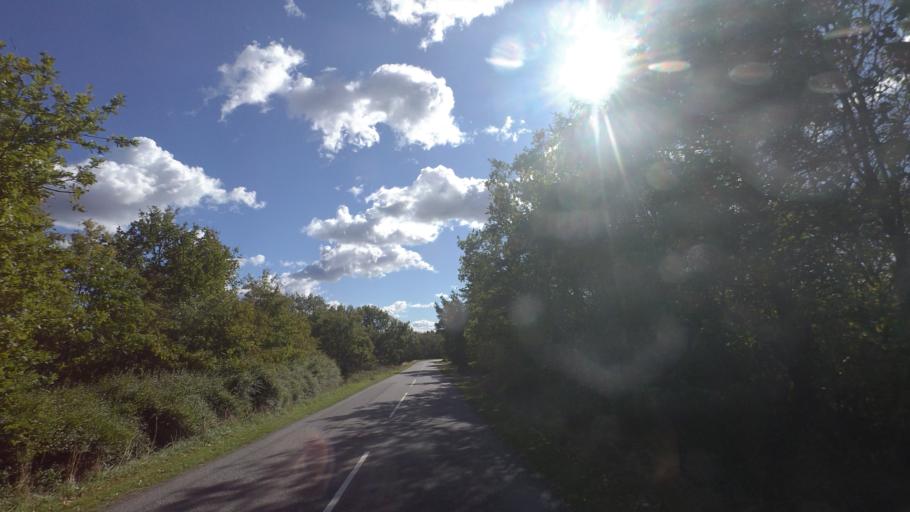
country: DK
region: Capital Region
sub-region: Bornholm Kommune
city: Nexo
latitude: 55.0688
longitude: 15.0828
